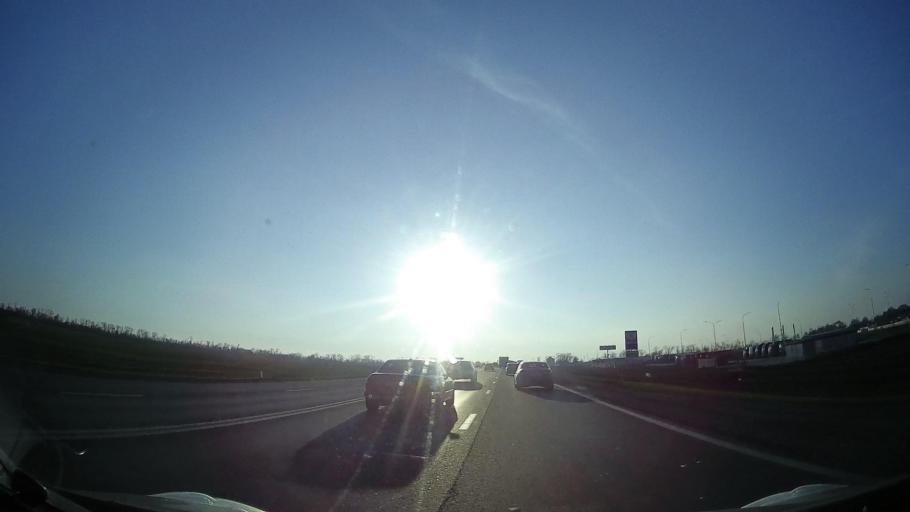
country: RU
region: Rostov
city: Bataysk
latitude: 47.0869
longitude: 39.7866
